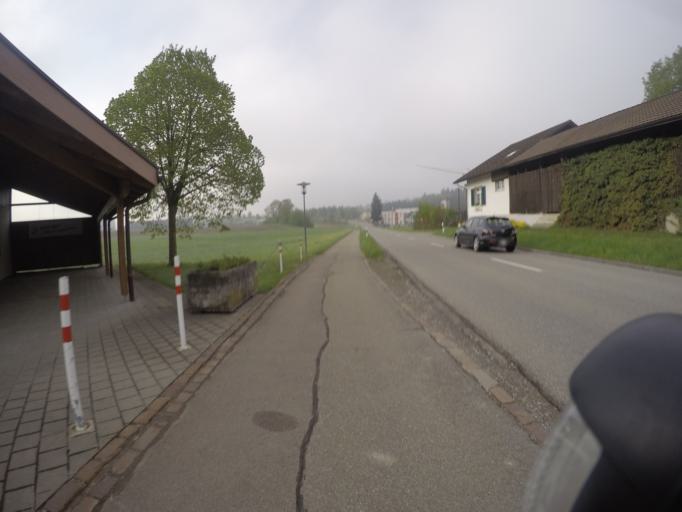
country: CH
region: Zurich
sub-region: Bezirk Pfaeffikon
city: Tagelswangen
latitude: 47.4414
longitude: 8.6819
